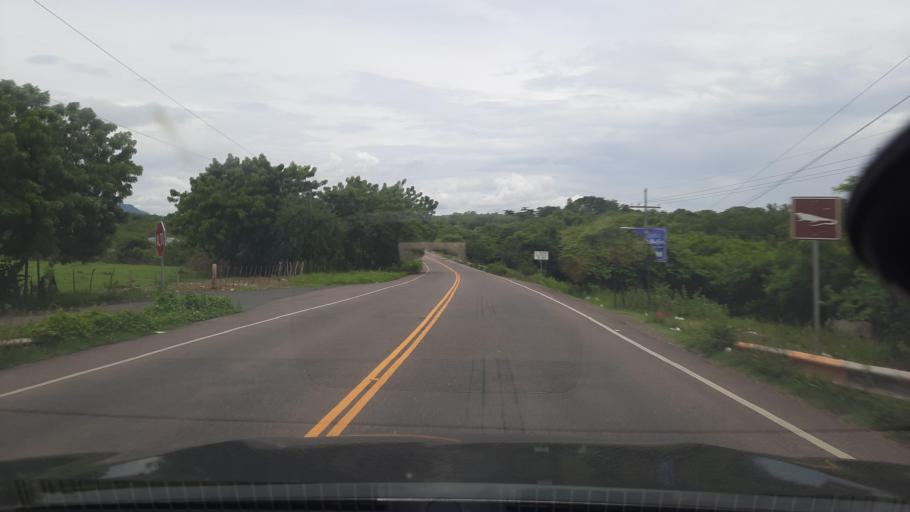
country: HN
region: Valle
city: Jicaro Galan
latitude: 13.5350
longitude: -87.4631
